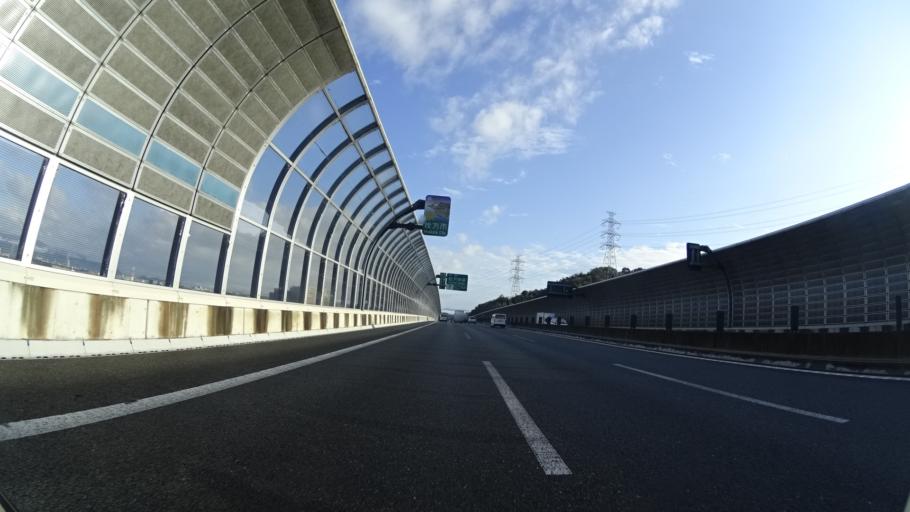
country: JP
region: Osaka
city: Hirakata
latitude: 34.7985
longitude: 135.7034
